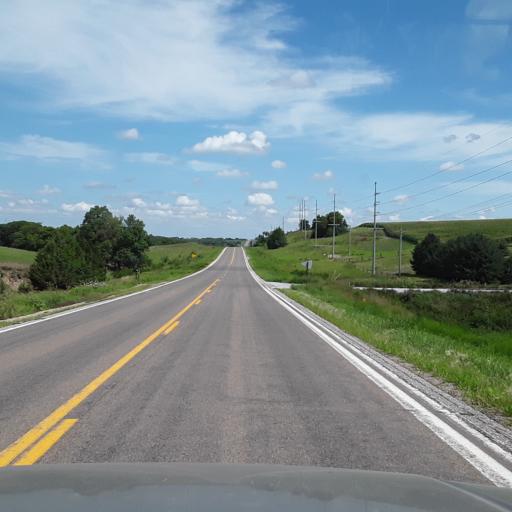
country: US
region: Nebraska
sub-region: York County
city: York
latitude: 40.9673
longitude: -97.4061
